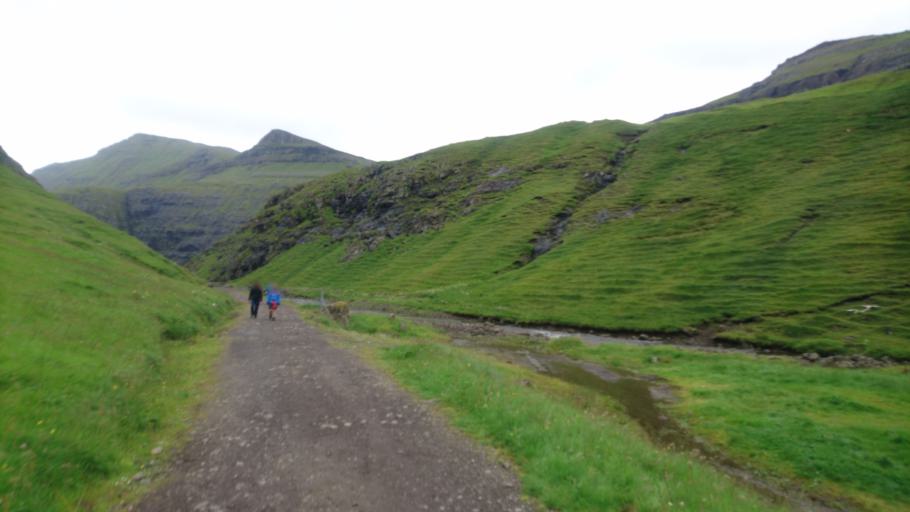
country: FO
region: Streymoy
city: Vestmanna
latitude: 62.2441
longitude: -7.1778
